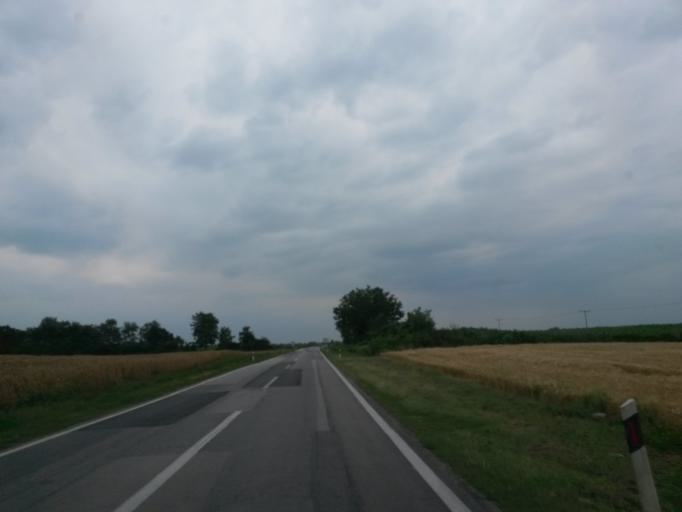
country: HR
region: Vukovarsko-Srijemska
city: Lovas
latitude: 45.2555
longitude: 19.1902
